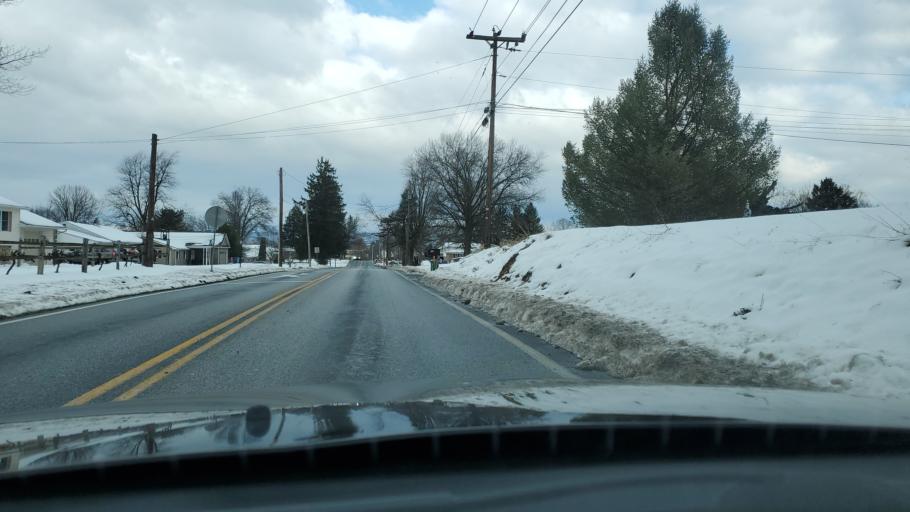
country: US
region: Pennsylvania
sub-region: Cumberland County
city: Mechanicsburg
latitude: 40.2231
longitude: -77.0543
